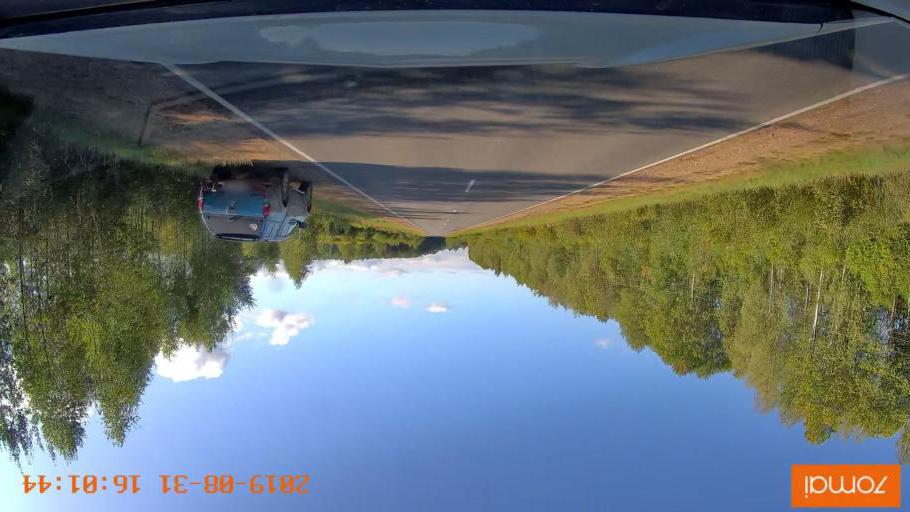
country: RU
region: Kaluga
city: Yukhnov
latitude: 54.6851
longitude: 35.2929
